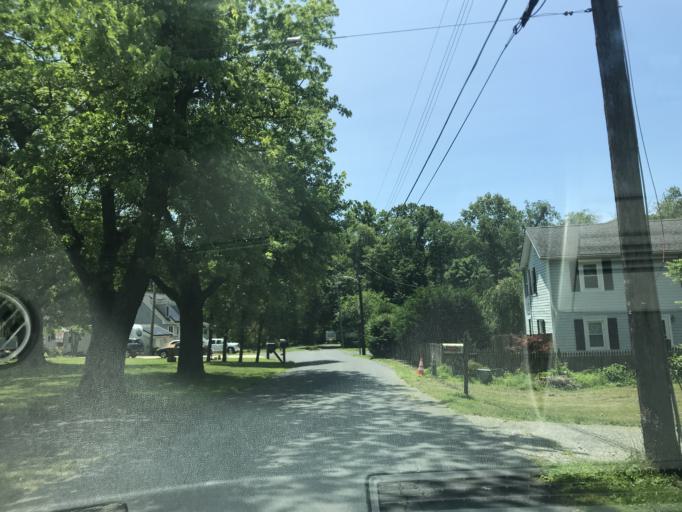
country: US
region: Maryland
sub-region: Harford County
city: Bel Air South
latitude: 39.5535
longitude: -76.2713
